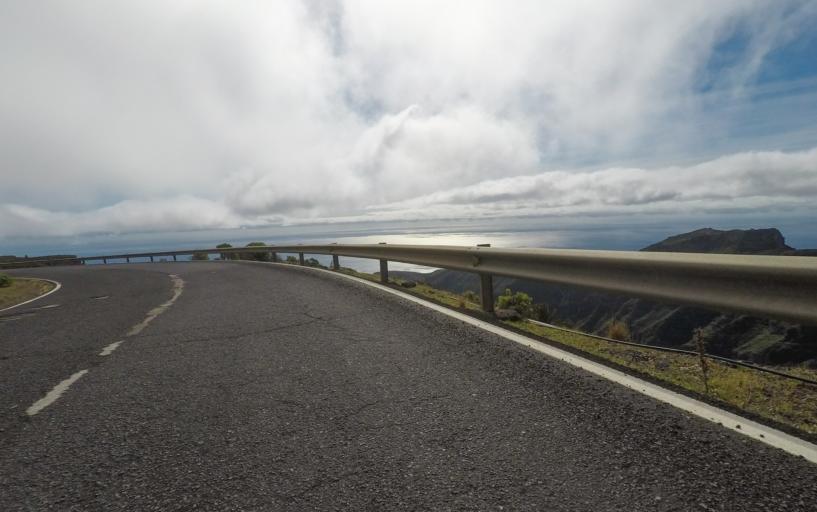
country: ES
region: Canary Islands
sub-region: Provincia de Santa Cruz de Tenerife
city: San Sebastian de la Gomera
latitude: 28.0978
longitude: -17.1795
